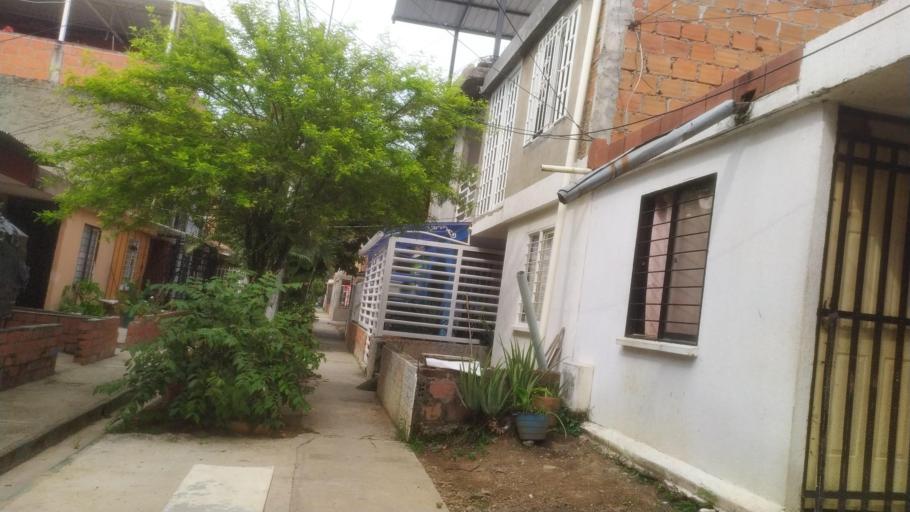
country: CO
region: Valle del Cauca
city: Jamundi
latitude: 3.2392
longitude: -76.5071
